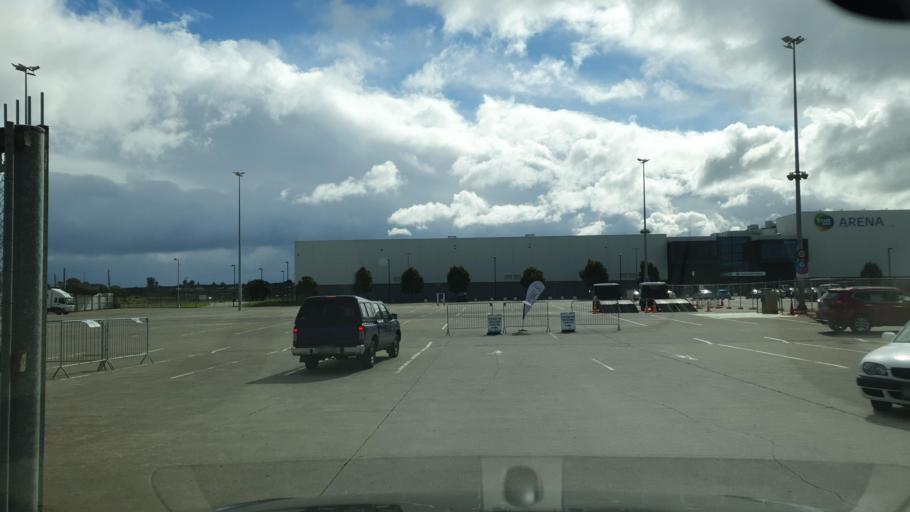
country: NZ
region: Bay of Plenty
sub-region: Tauranga City
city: Tauranga
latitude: -37.6867
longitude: 176.2253
